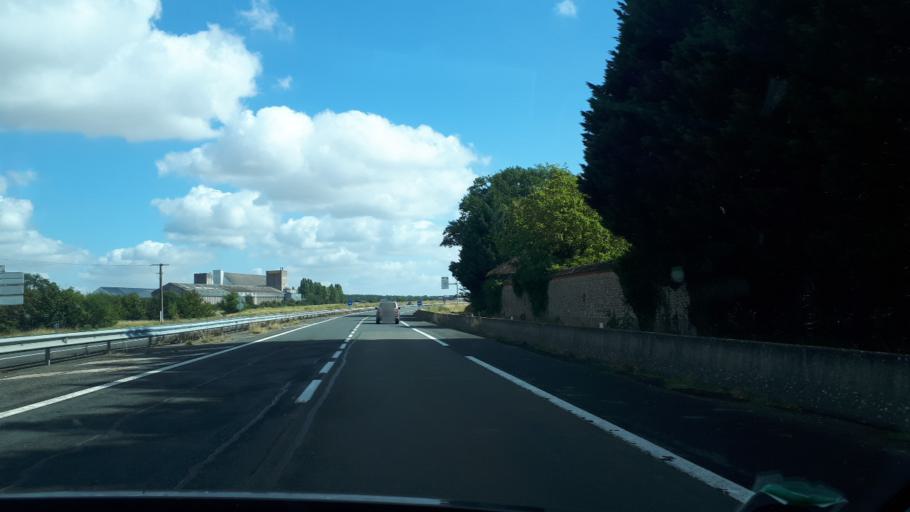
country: FR
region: Centre
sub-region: Departement du Loir-et-Cher
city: Saint-Ouen
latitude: 47.8424
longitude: 1.0921
